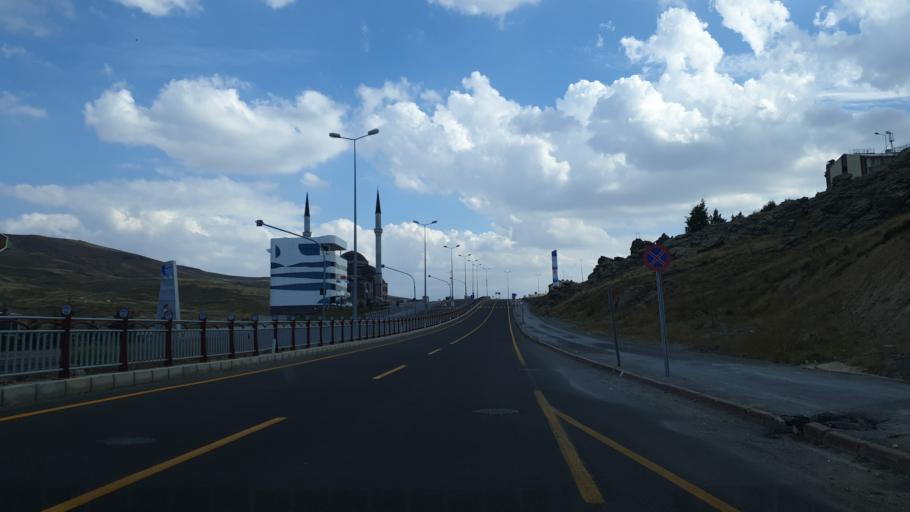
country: TR
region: Kayseri
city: Hacilar
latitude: 38.5430
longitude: 35.5270
